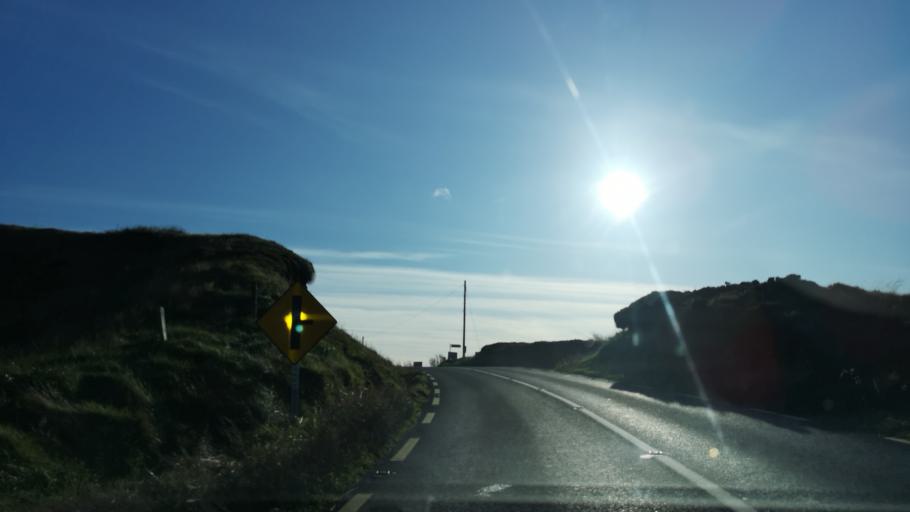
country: IE
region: Connaught
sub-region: County Galway
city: Clifden
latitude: 53.5410
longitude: -10.0295
